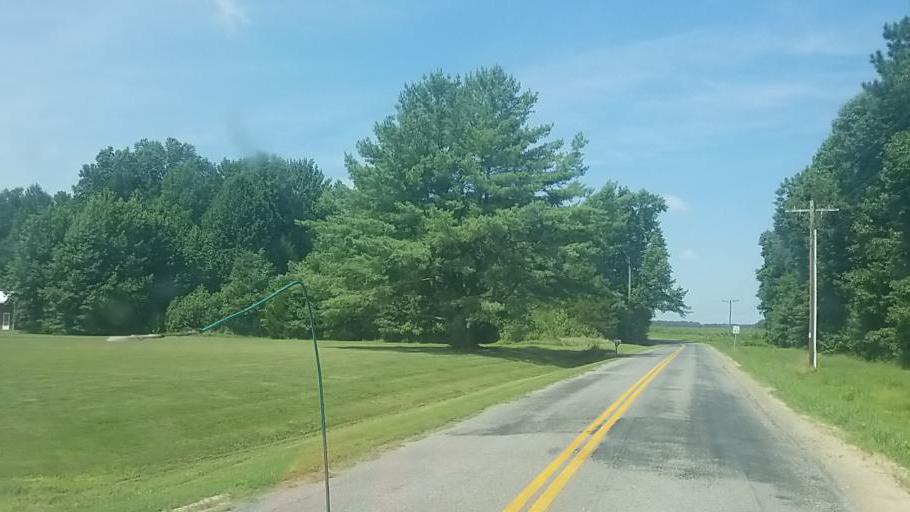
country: US
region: Maryland
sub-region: Caroline County
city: Denton
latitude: 38.8715
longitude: -75.7480
